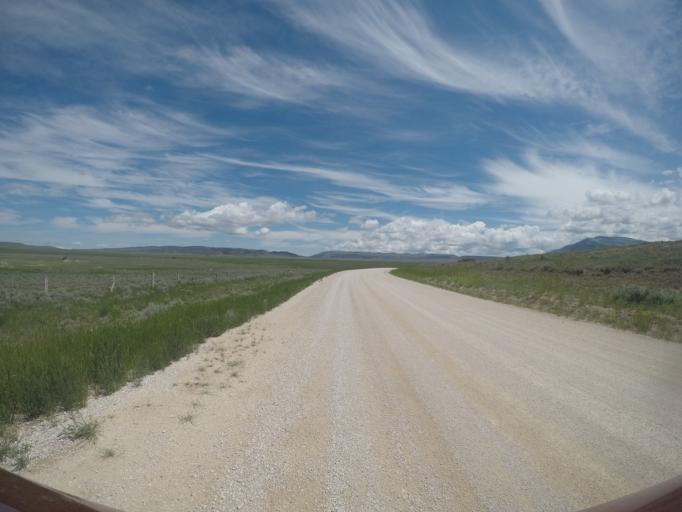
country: US
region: Wyoming
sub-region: Park County
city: Powell
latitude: 45.2066
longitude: -108.7299
